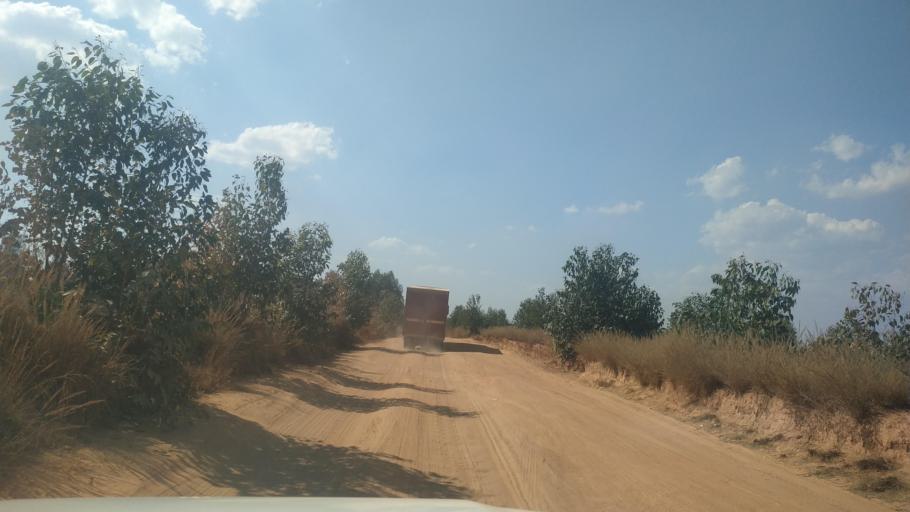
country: MG
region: Alaotra Mangoro
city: Ambatondrazaka
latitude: -18.0423
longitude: 48.2494
